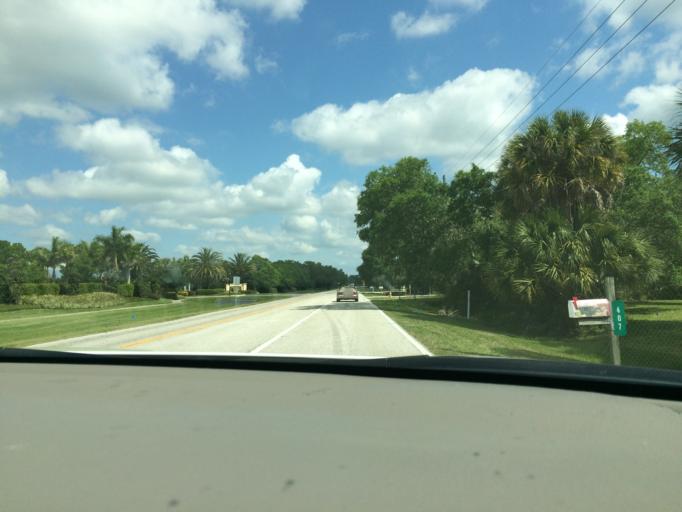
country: US
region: Florida
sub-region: Manatee County
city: Ellenton
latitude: 27.5073
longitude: -82.4336
